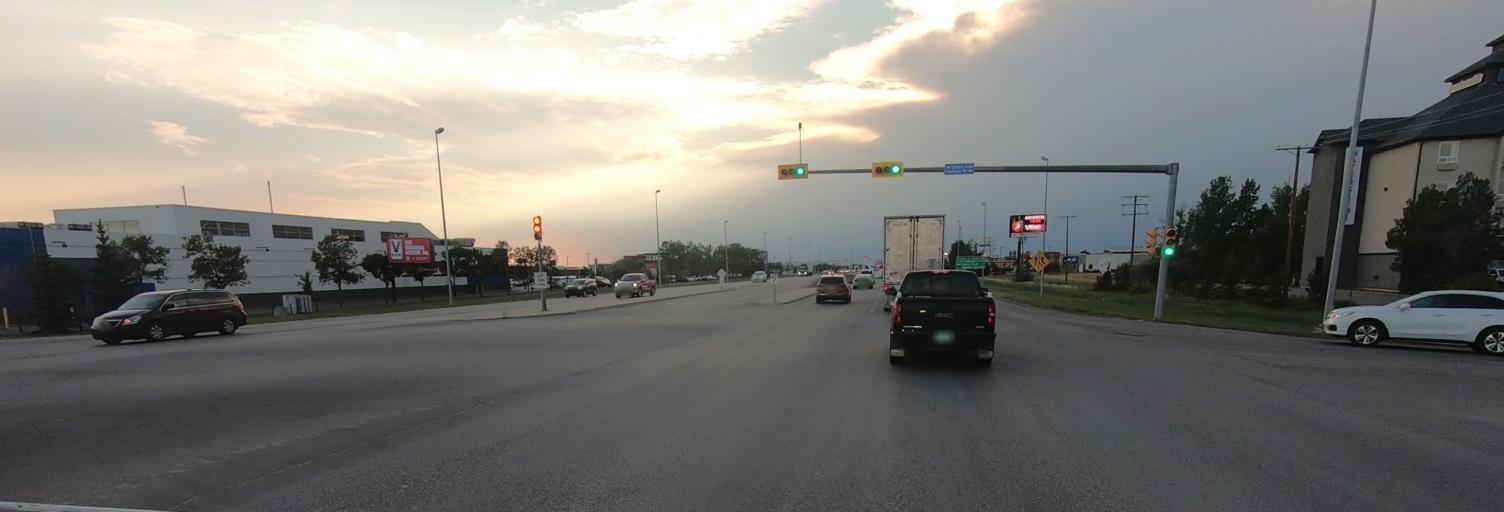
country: CA
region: Saskatchewan
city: Regina
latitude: 50.4478
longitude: -104.5272
